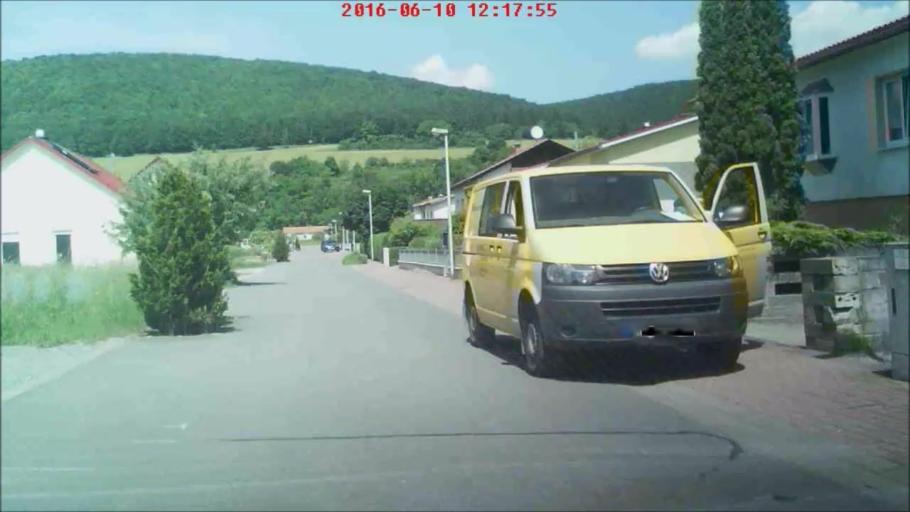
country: DE
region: Thuringia
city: Obermassfeld-Grimmenthal
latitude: 50.5297
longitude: 10.4498
